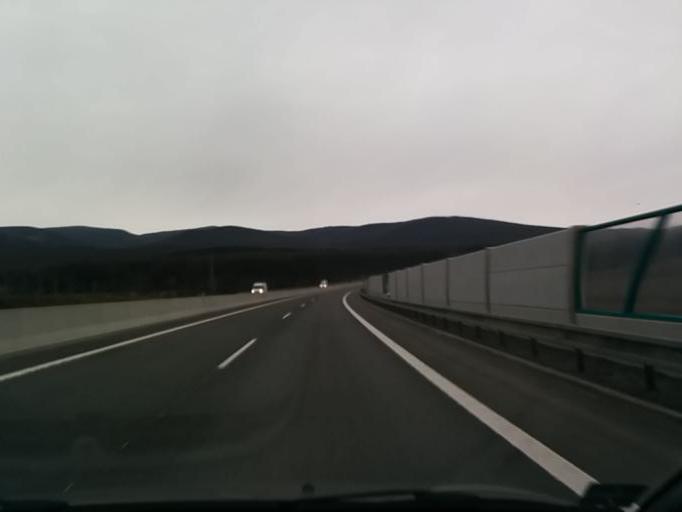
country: SK
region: Nitriansky
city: Tlmace
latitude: 48.3686
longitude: 18.5040
